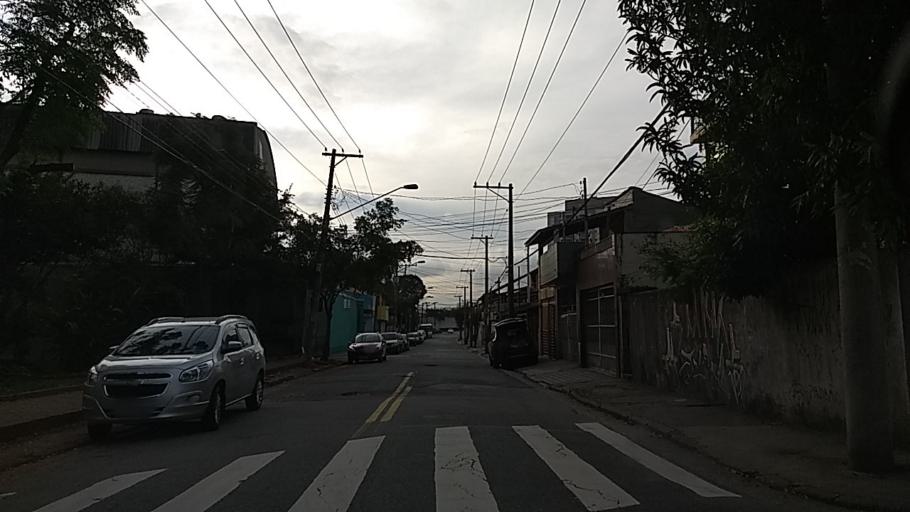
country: BR
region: Sao Paulo
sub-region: Sao Paulo
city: Sao Paulo
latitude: -23.5274
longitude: -46.6024
